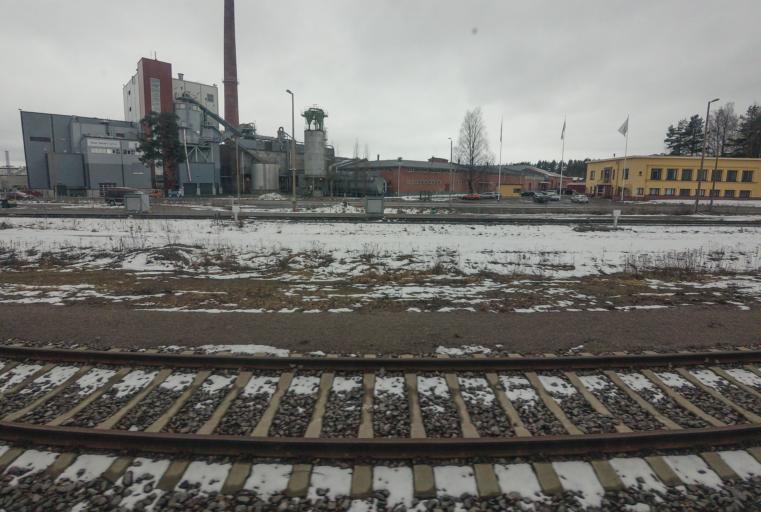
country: FI
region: Southern Savonia
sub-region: Savonlinna
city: Savonlinna
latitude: 61.8628
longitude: 28.9205
